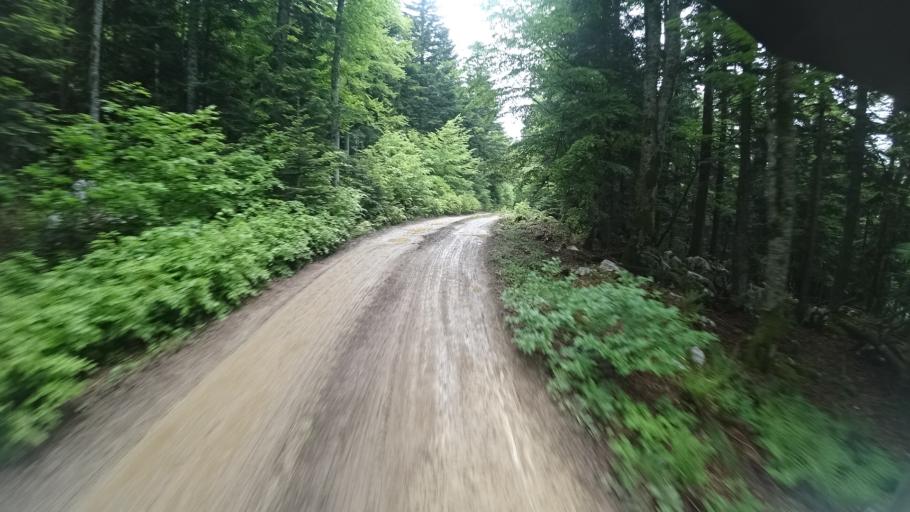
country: BA
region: Federation of Bosnia and Herzegovina
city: Bihac
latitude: 44.7018
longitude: 15.8328
